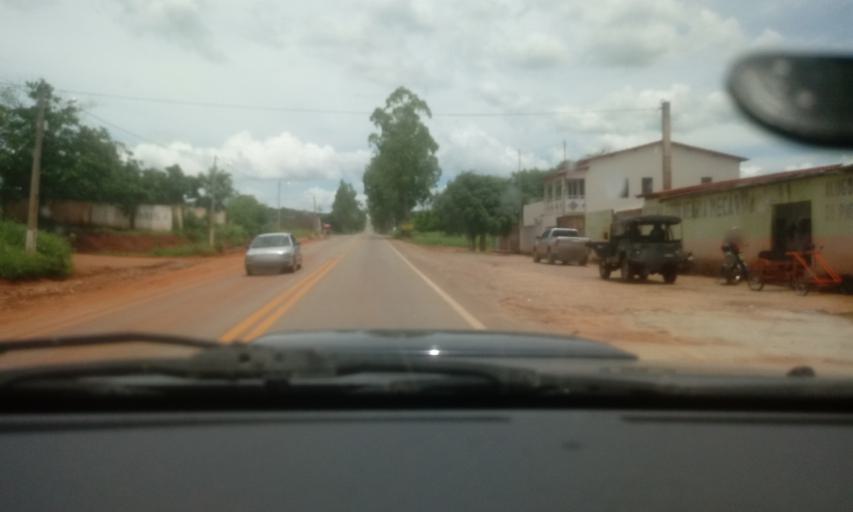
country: BR
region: Bahia
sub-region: Riacho De Santana
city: Riacho de Santana
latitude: -13.6023
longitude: -42.9404
